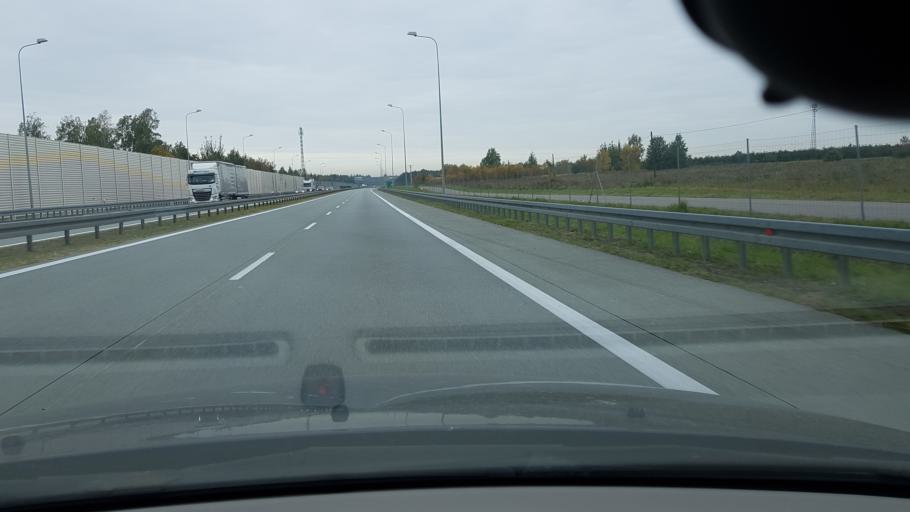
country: PL
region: Lodz Voivodeship
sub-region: Powiat skierniewicki
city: Kowiesy
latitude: 51.8945
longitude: 20.4255
